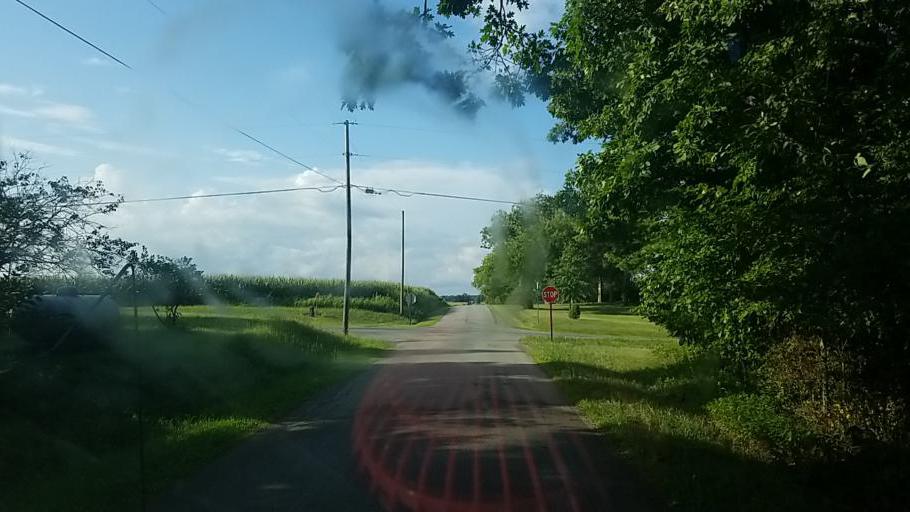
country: US
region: Ohio
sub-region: Wyandot County
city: Upper Sandusky
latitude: 40.8258
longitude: -83.1601
